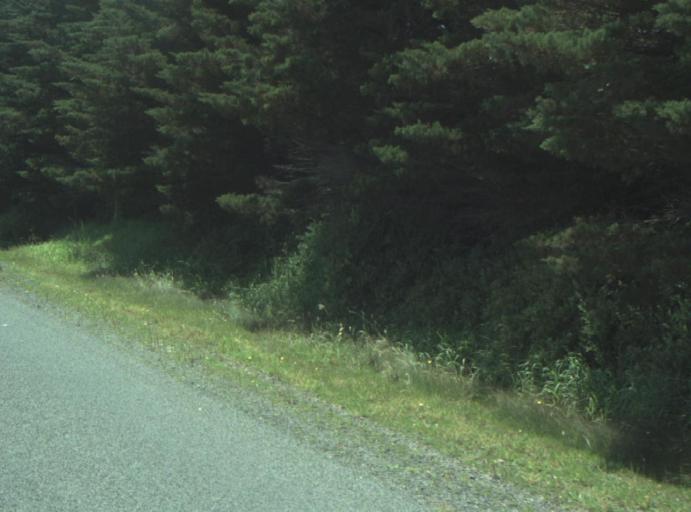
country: AU
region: Victoria
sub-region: Greater Geelong
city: Leopold
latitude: -38.2713
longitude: 144.4378
